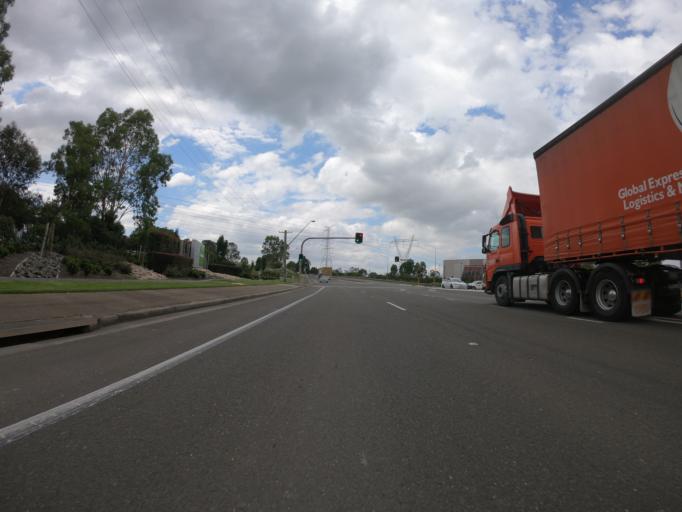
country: AU
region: New South Wales
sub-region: Blacktown
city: Mount Druitt
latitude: -33.8129
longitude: 150.7856
